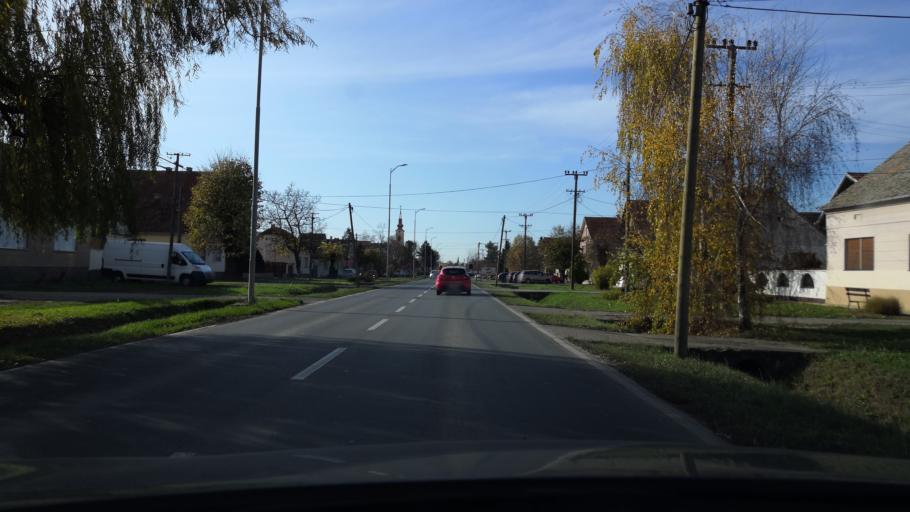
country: RS
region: Autonomna Pokrajina Vojvodina
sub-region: Sremski Okrug
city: Stara Pazova
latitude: 44.9866
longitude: 20.1748
